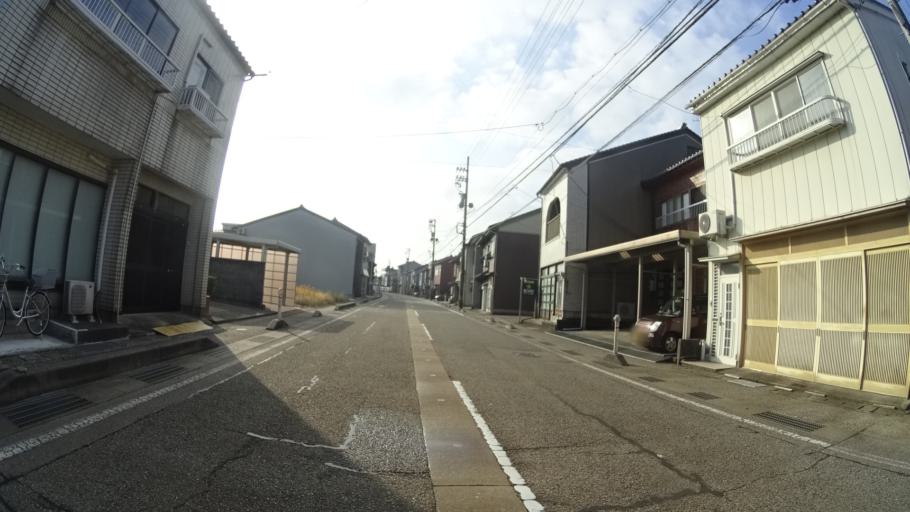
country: JP
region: Toyama
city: Himi
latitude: 36.8693
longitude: 136.9831
